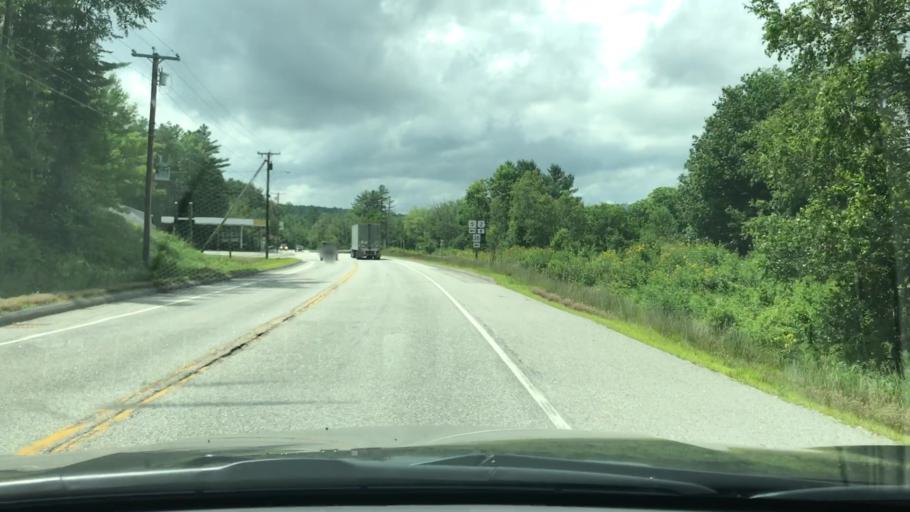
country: US
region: Maine
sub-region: Oxford County
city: Bethel
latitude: 44.4096
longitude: -70.8022
